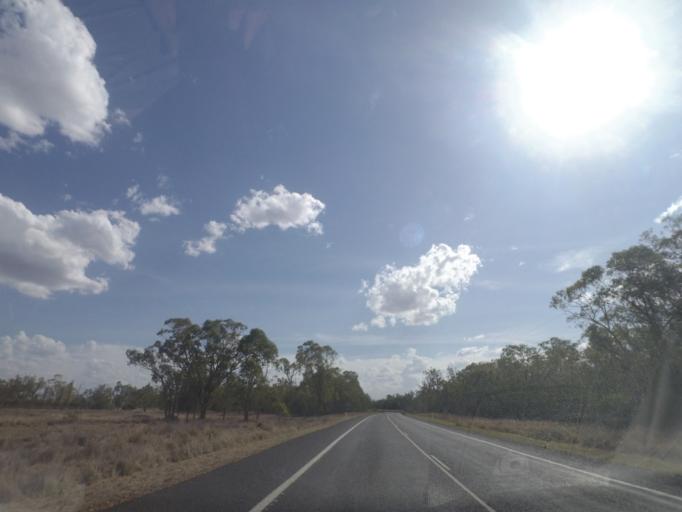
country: AU
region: New South Wales
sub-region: Moree Plains
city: Boggabilla
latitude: -28.5364
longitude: 150.8912
